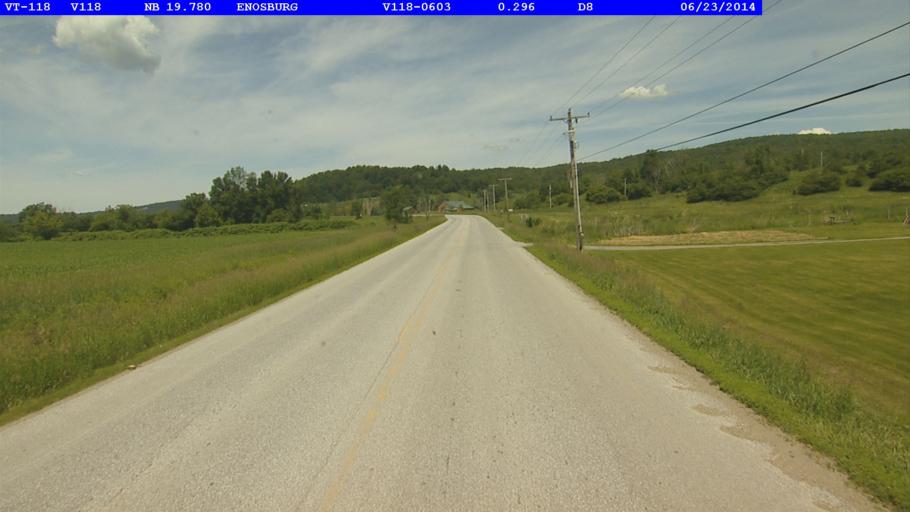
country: US
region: Vermont
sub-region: Franklin County
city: Richford
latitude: 44.9243
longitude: -72.6759
